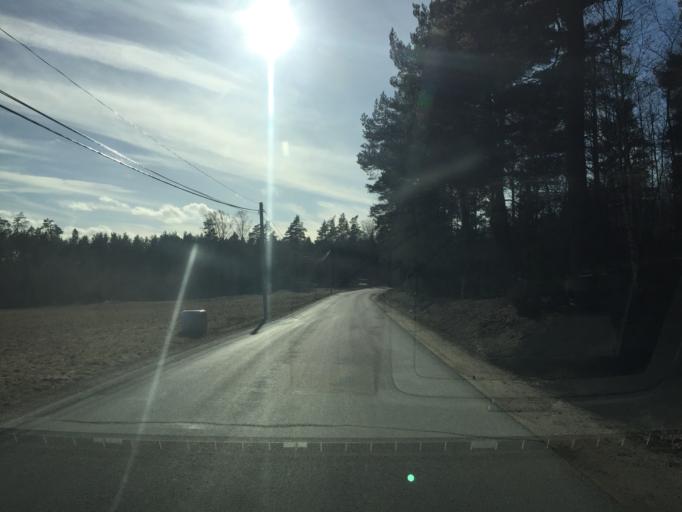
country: SE
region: Stockholm
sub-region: Nynashamns Kommun
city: Osmo
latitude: 59.0528
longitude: 17.8626
